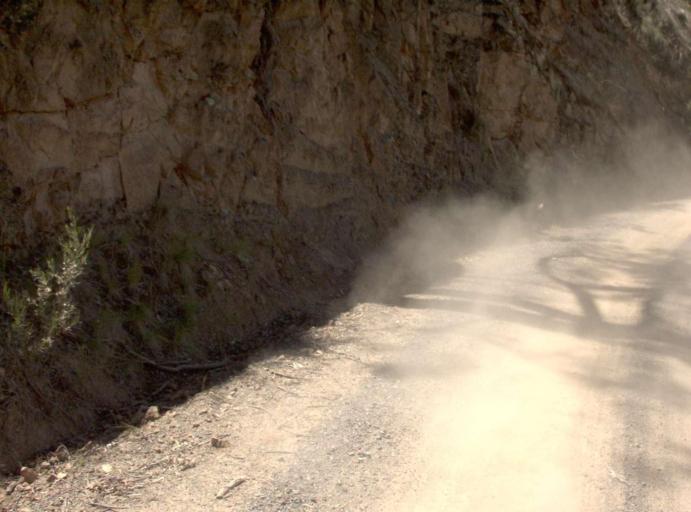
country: AU
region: New South Wales
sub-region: Snowy River
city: Jindabyne
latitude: -37.0389
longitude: 148.5547
